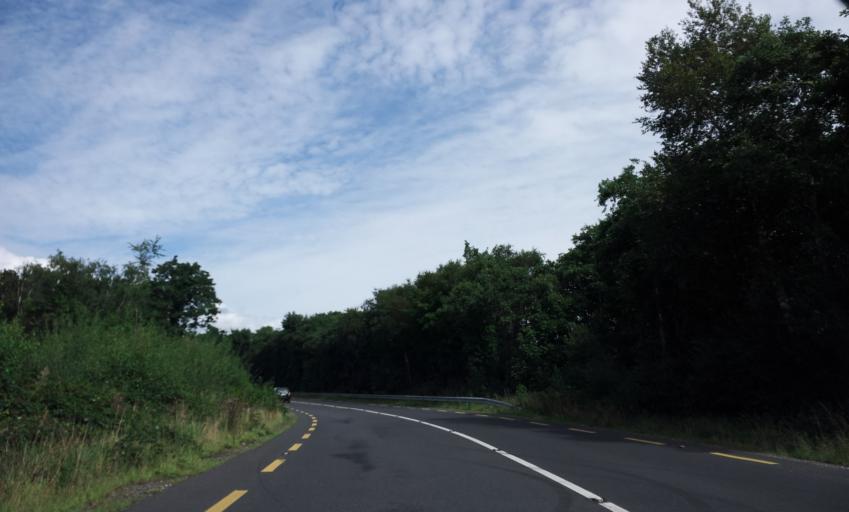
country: IE
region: Munster
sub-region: Ciarrai
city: Killorglin
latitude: 52.0986
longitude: -9.8263
